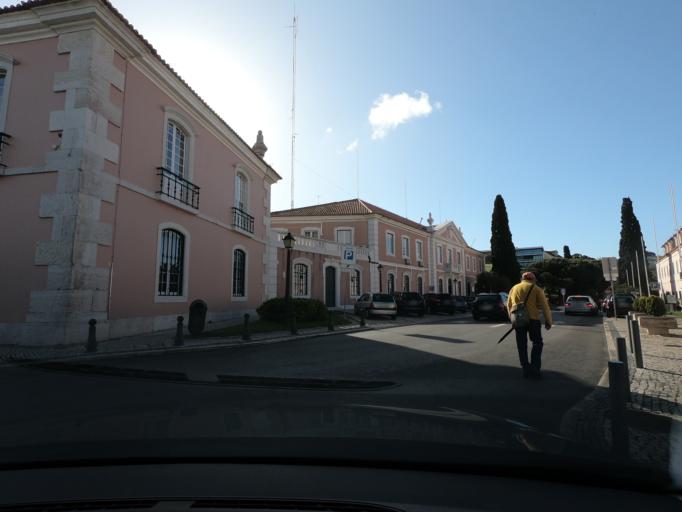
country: PT
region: Lisbon
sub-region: Oeiras
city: Oeiras
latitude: 38.6927
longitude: -9.3144
